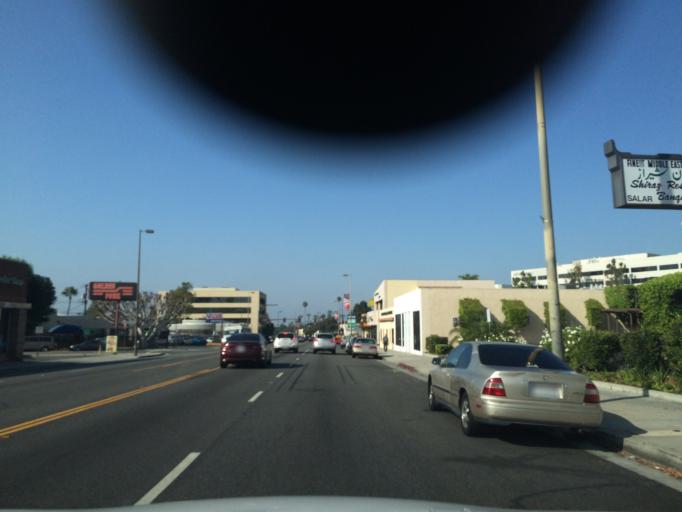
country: US
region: California
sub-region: Los Angeles County
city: Glendale
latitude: 34.1443
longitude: -118.2482
